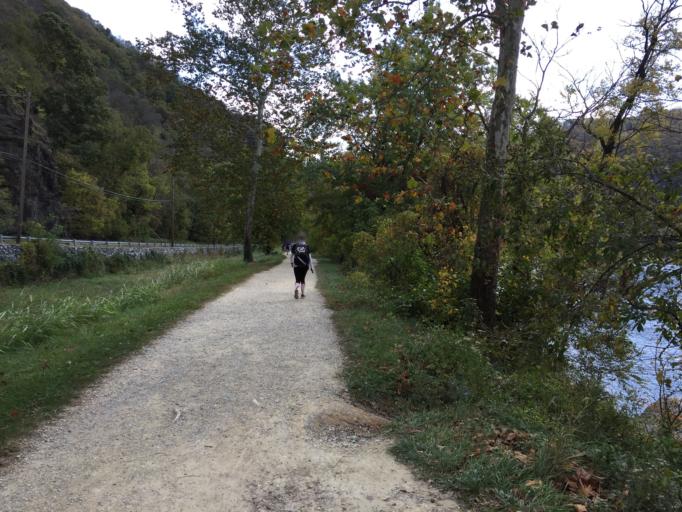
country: US
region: West Virginia
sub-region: Jefferson County
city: Bolivar
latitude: 39.3277
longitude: -77.7296
